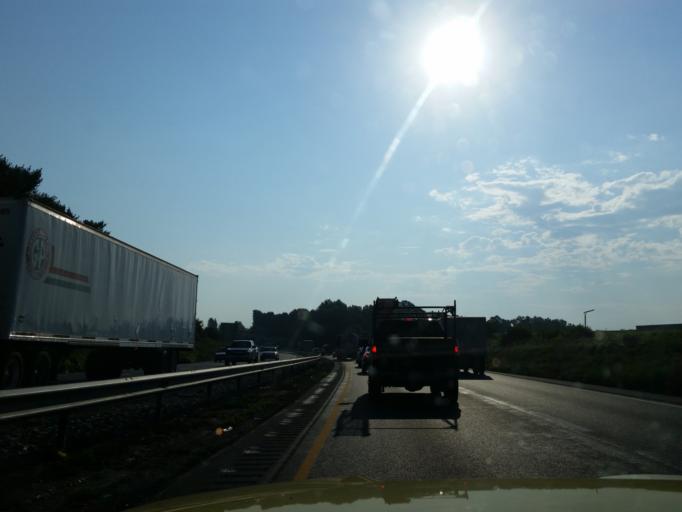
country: US
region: Pennsylvania
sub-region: Lancaster County
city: East Petersburg
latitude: 40.0527
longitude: -76.3766
